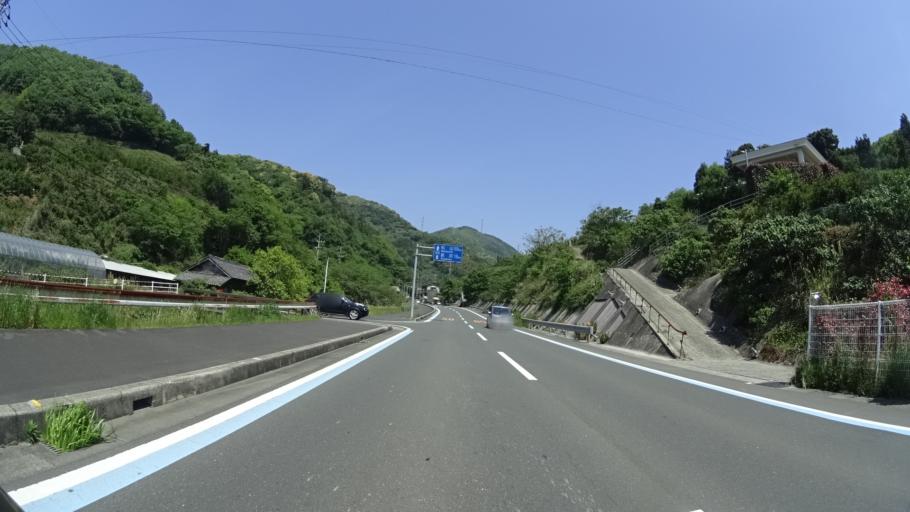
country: JP
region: Ehime
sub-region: Nishiuwa-gun
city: Ikata-cho
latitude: 33.4984
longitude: 132.3972
